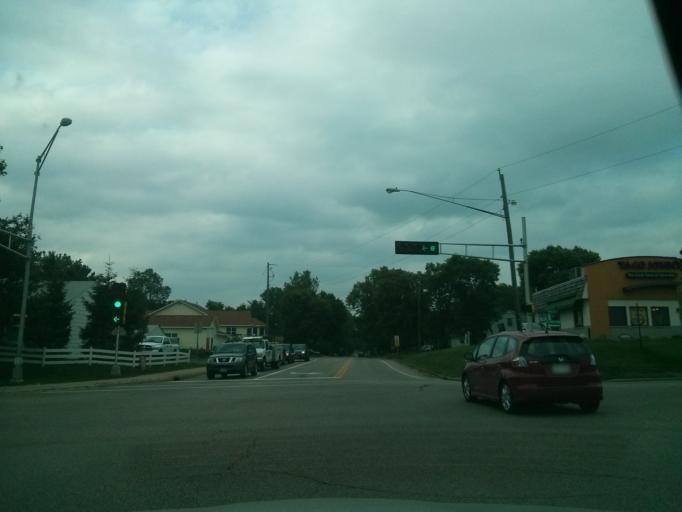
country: US
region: Wisconsin
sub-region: Saint Croix County
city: Hudson
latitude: 44.9632
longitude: -92.7436
